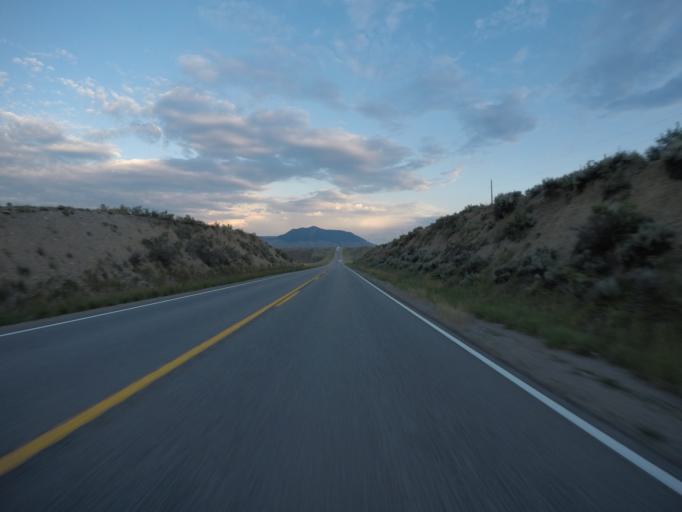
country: US
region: Colorado
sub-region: Grand County
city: Kremmling
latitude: 40.1749
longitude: -106.4197
